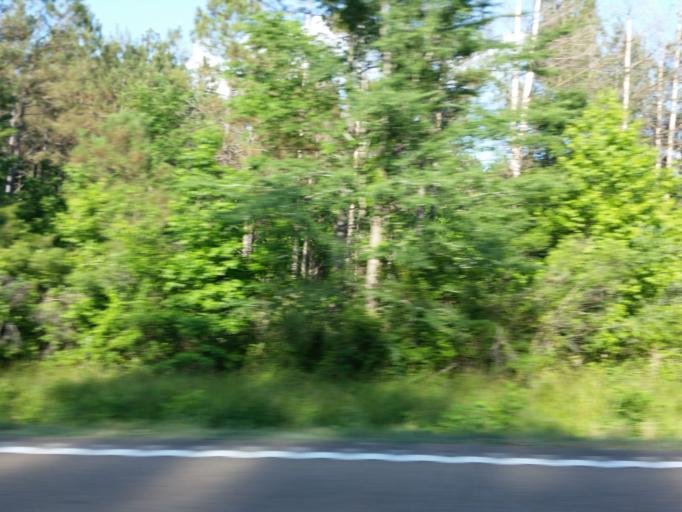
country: US
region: Mississippi
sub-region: Calhoun County
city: Calhoun City
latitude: 33.7786
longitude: -89.3641
